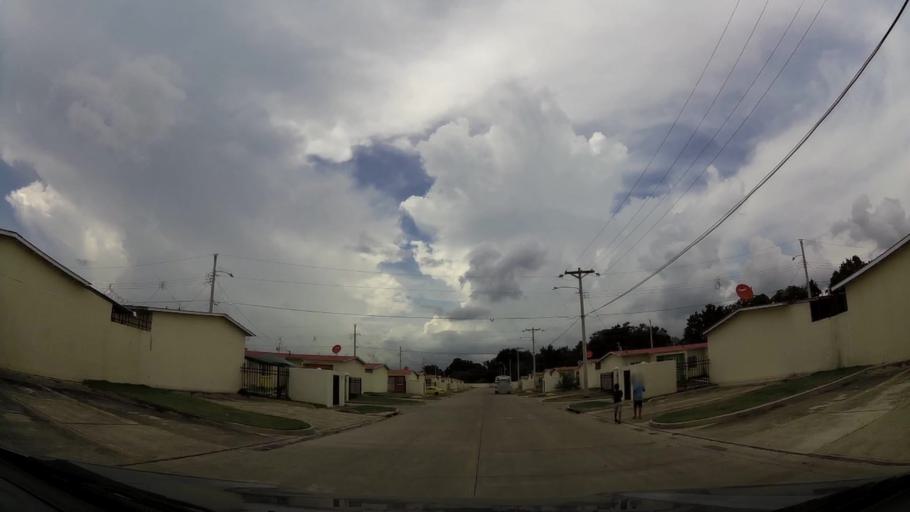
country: PA
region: Panama
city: Cabra Numero Uno
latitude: 9.1221
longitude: -79.3200
